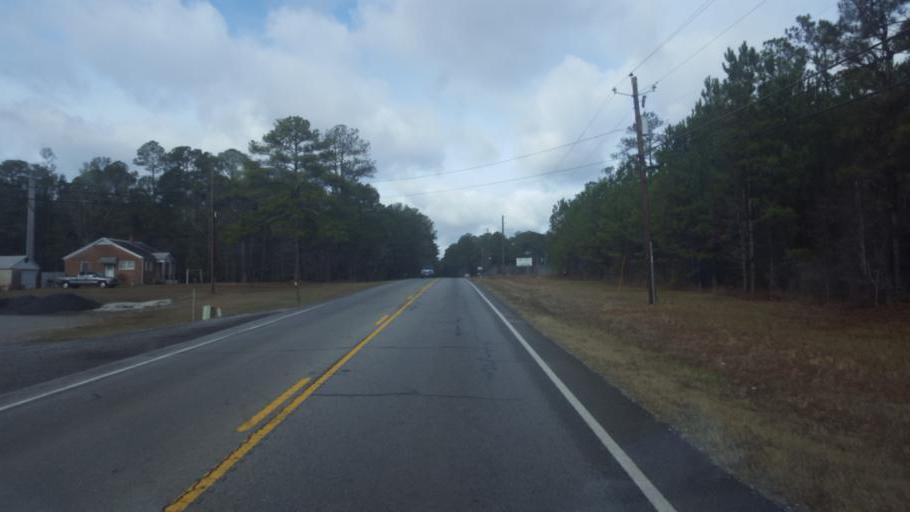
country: US
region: Georgia
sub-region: Butts County
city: Indian Springs
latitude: 33.2804
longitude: -83.9228
